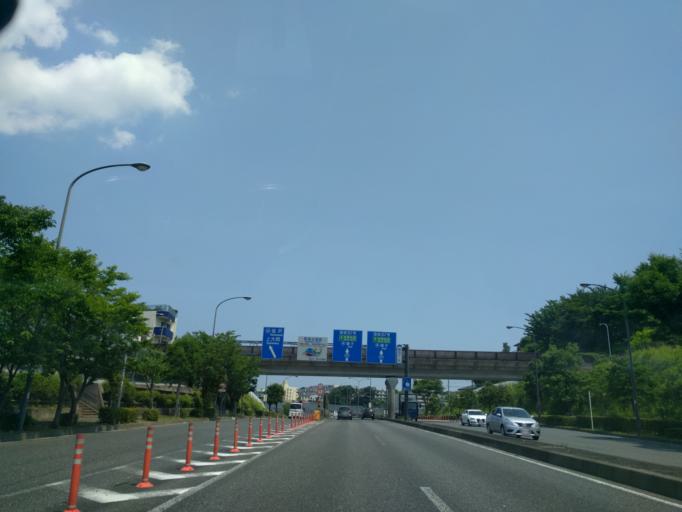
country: JP
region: Kanagawa
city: Yokohama
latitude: 35.3931
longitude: 139.5966
